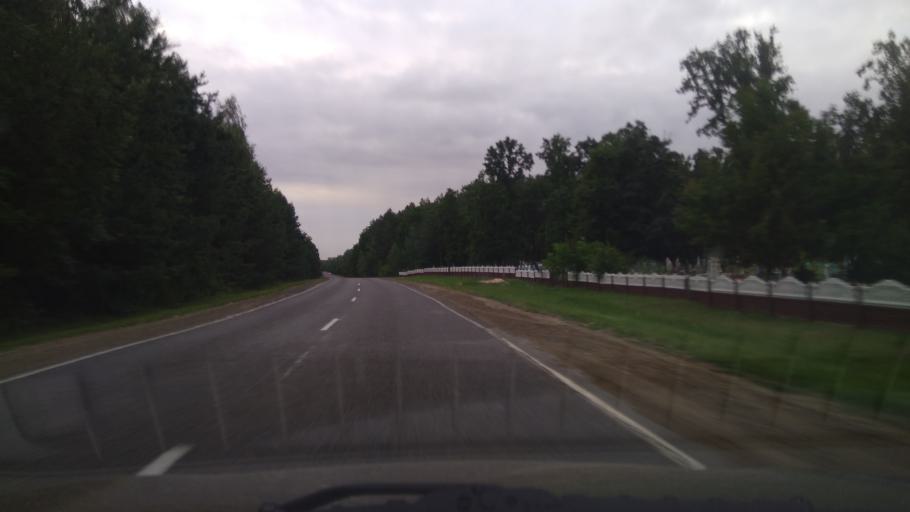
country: BY
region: Brest
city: Byaroza
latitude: 52.4049
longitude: 25.0002
